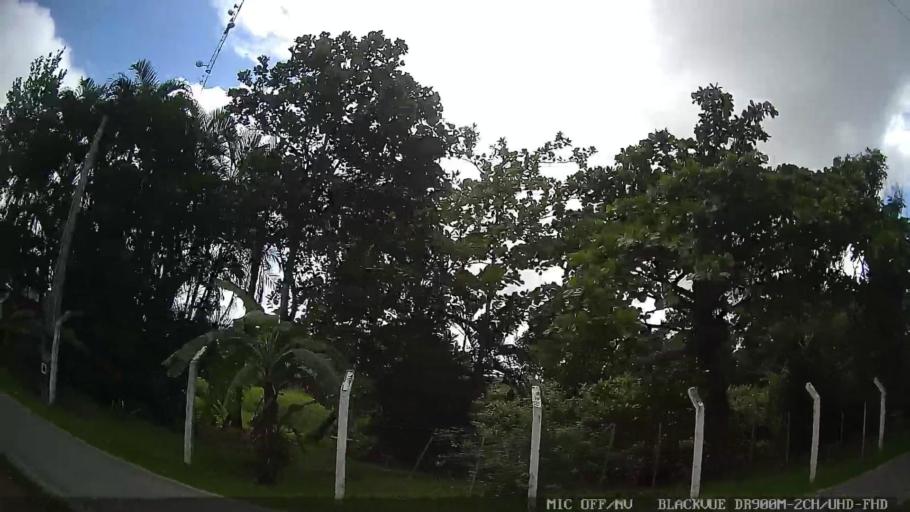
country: BR
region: Sao Paulo
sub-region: Peruibe
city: Peruibe
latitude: -24.3056
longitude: -47.0142
